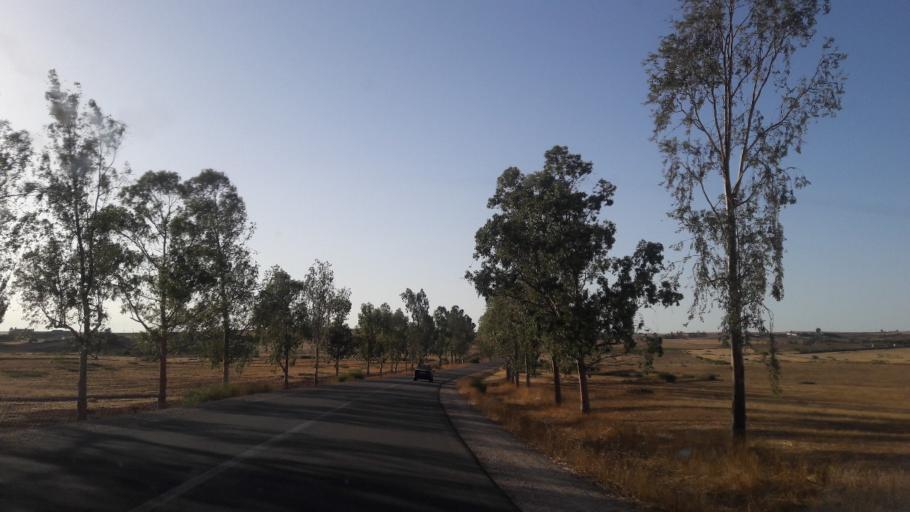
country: MA
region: Chaouia-Ouardigha
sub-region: Khouribga Province
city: Boujniba
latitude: 33.0128
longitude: -6.6915
